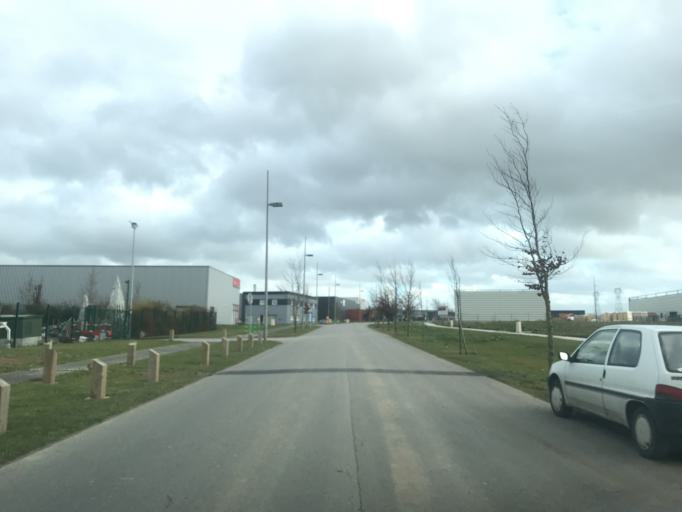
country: FR
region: Lower Normandy
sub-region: Departement du Calvados
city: Cormelles-le-Royal
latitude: 49.1441
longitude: -0.3342
